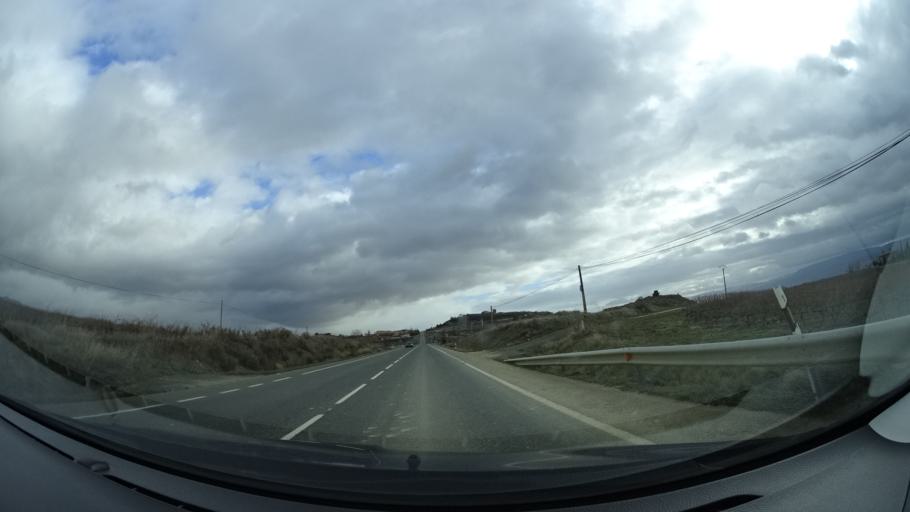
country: ES
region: Basque Country
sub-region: Provincia de Alava
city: Laguardia
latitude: 42.5644
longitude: -2.6008
